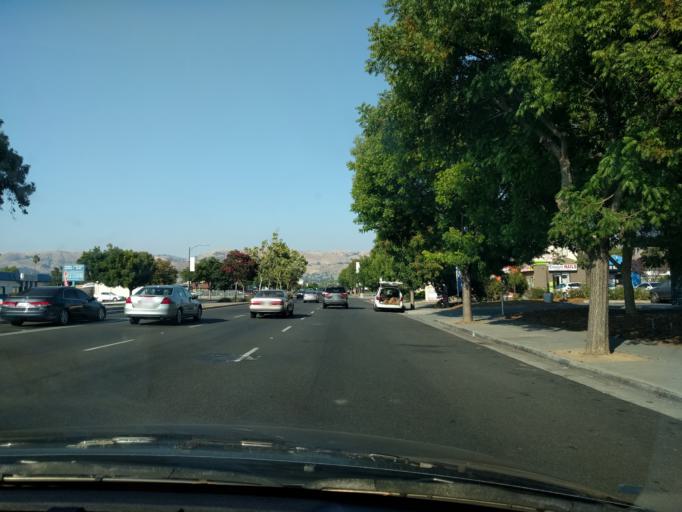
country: US
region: California
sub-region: Santa Clara County
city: Alum Rock
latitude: 37.3448
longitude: -121.8356
